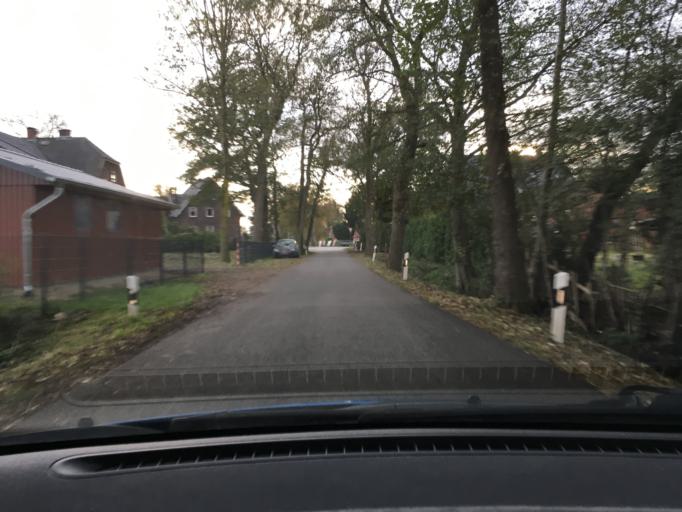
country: DE
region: Hamburg
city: Harburg
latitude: 53.4469
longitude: 10.0350
